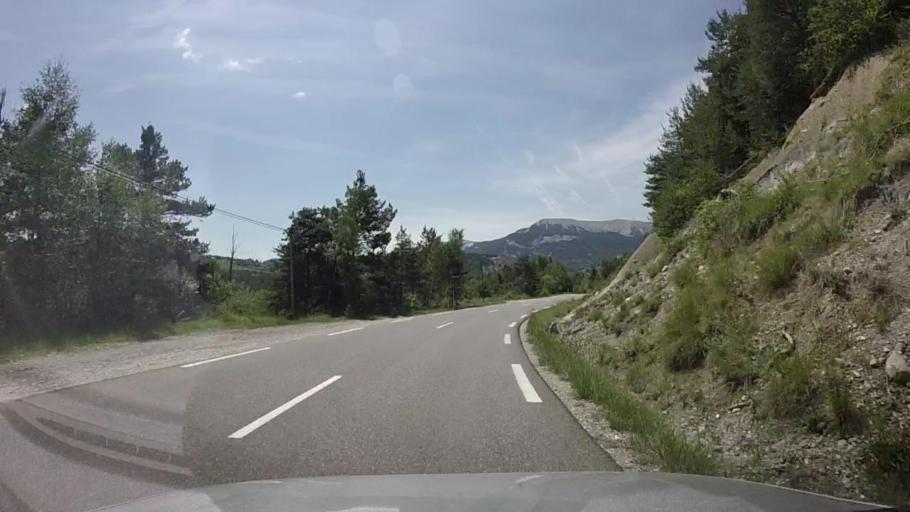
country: FR
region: Provence-Alpes-Cote d'Azur
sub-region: Departement des Alpes-de-Haute-Provence
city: Seyne-les-Alpes
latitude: 44.3863
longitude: 6.3289
